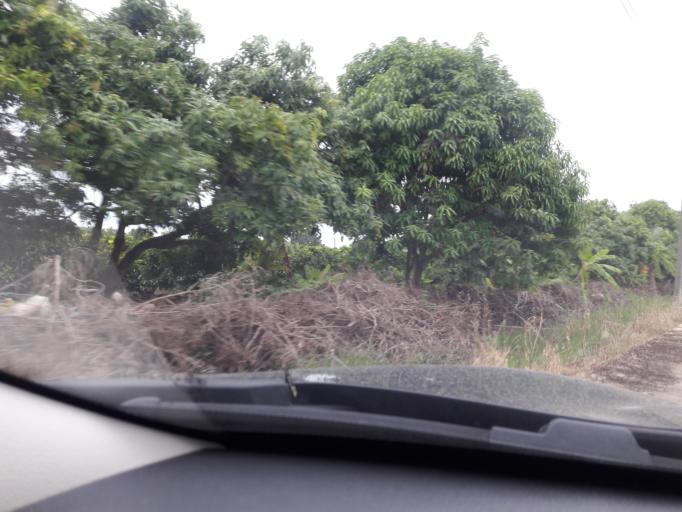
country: TH
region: Ratchaburi
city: Bang Phae
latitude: 13.6296
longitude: 99.9428
